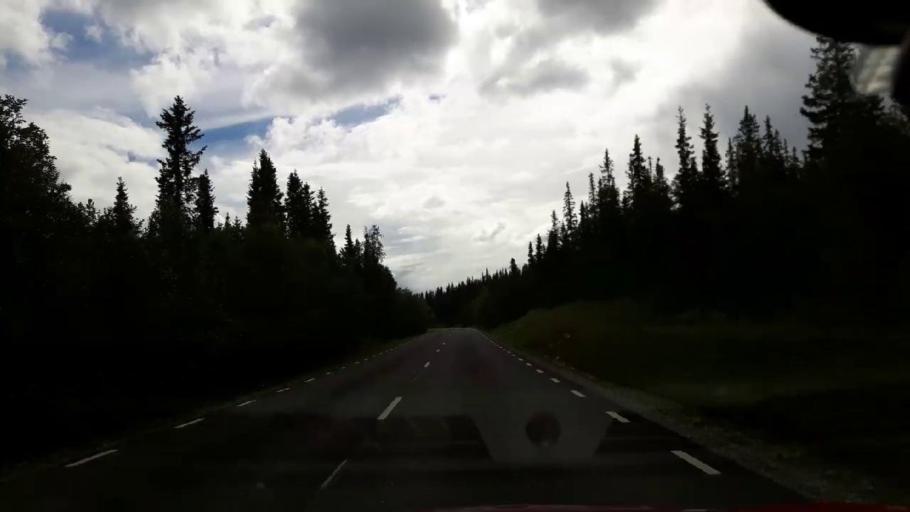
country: NO
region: Nord-Trondelag
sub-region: Royrvik
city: Royrvik
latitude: 64.8108
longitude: 14.0666
